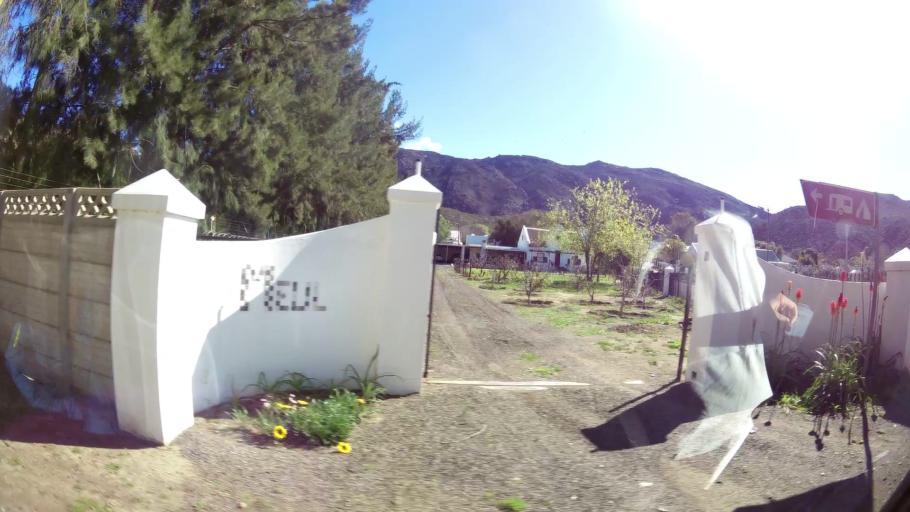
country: ZA
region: Western Cape
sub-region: Cape Winelands District Municipality
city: Ashton
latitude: -33.7859
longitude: 20.1149
